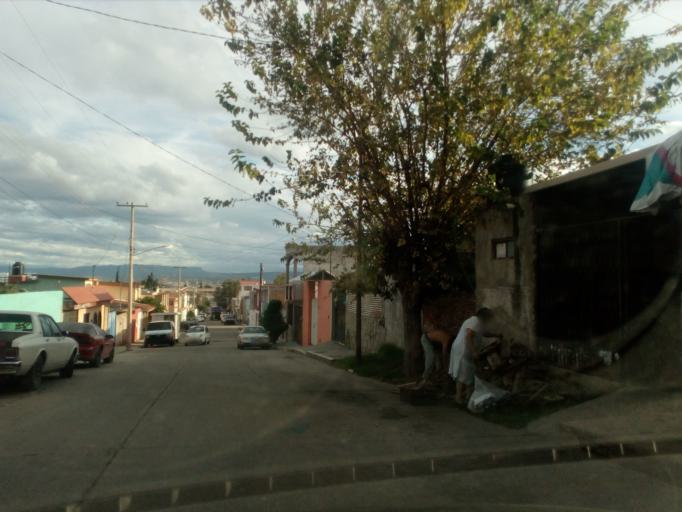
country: MX
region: Durango
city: Victoria de Durango
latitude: 24.0435
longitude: -104.6658
